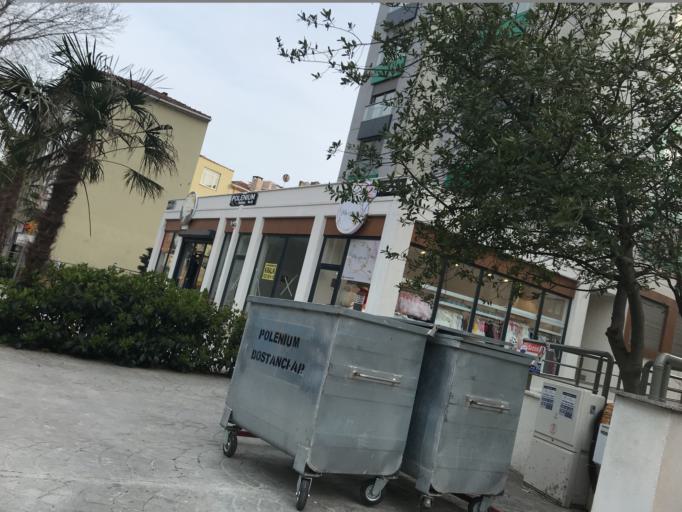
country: TR
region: Istanbul
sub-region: Atasehir
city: Atasehir
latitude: 40.9550
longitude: 29.0934
